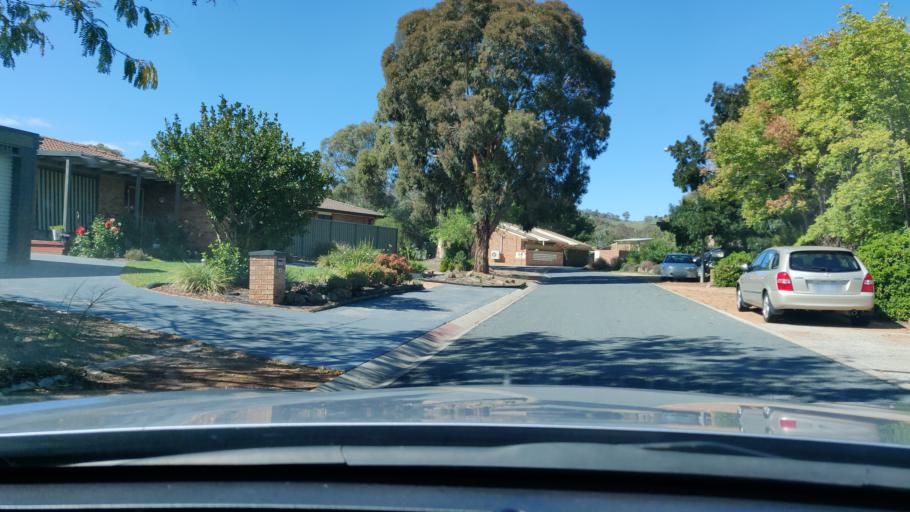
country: AU
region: Australian Capital Territory
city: Macarthur
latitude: -35.4399
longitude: 149.0948
